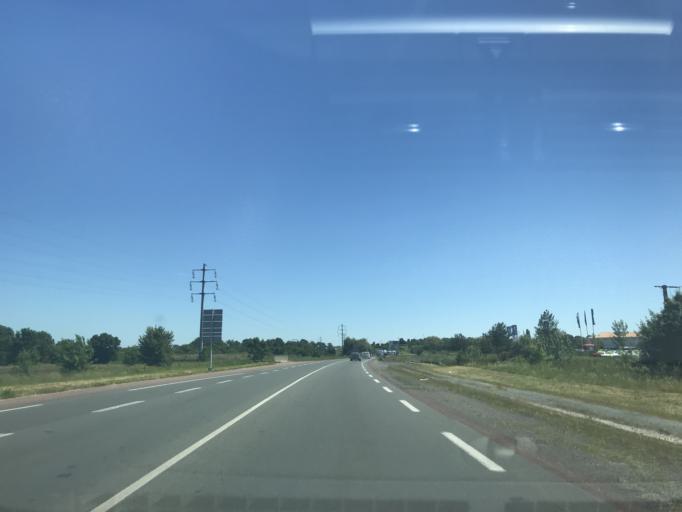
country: FR
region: Poitou-Charentes
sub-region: Departement de la Charente-Maritime
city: Saint-Georges-de-Didonne
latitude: 45.6190
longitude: -0.9914
